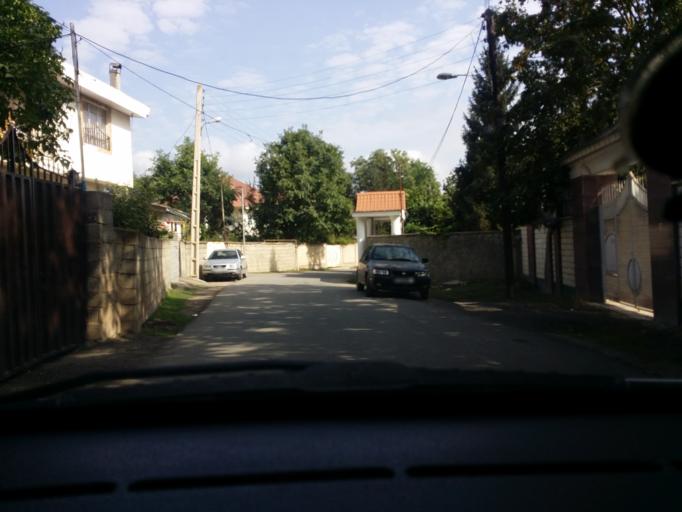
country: IR
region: Mazandaran
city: `Abbasabad
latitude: 36.5069
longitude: 51.1877
